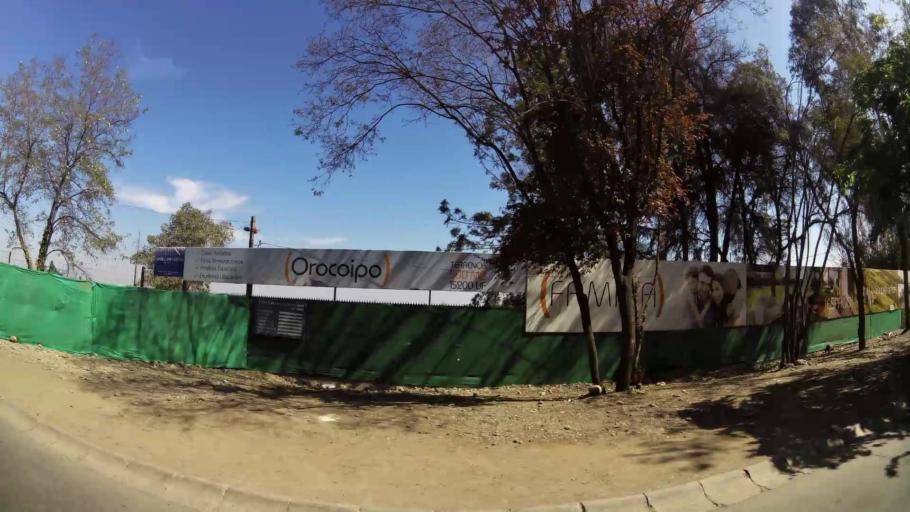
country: CL
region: Santiago Metropolitan
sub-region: Provincia de Santiago
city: Villa Presidente Frei, Nunoa, Santiago, Chile
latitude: -33.4359
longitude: -70.5183
